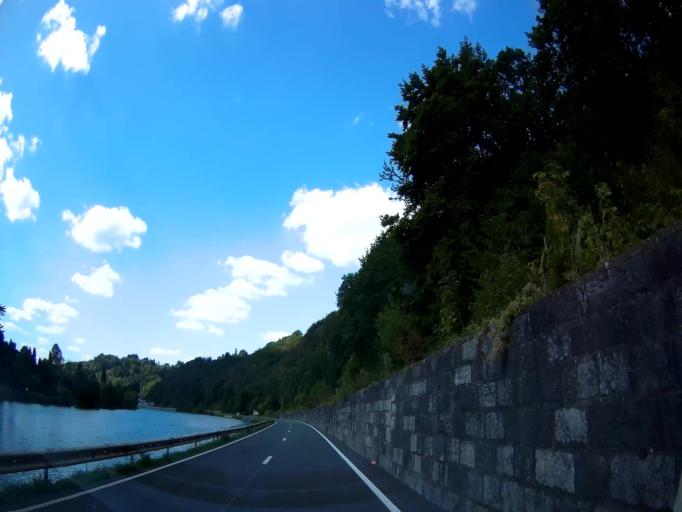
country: BE
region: Wallonia
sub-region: Province de Namur
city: Hastiere-Lavaux
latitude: 50.2156
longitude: 4.8410
